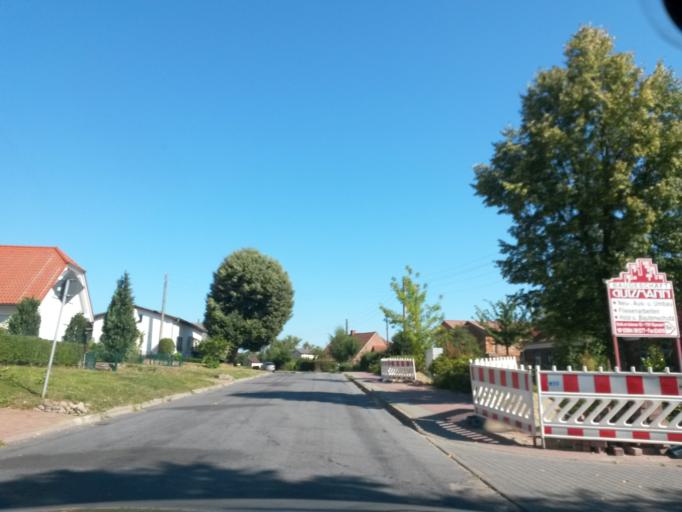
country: DE
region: Brandenburg
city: Prenzlau
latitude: 53.2825
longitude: 13.8449
